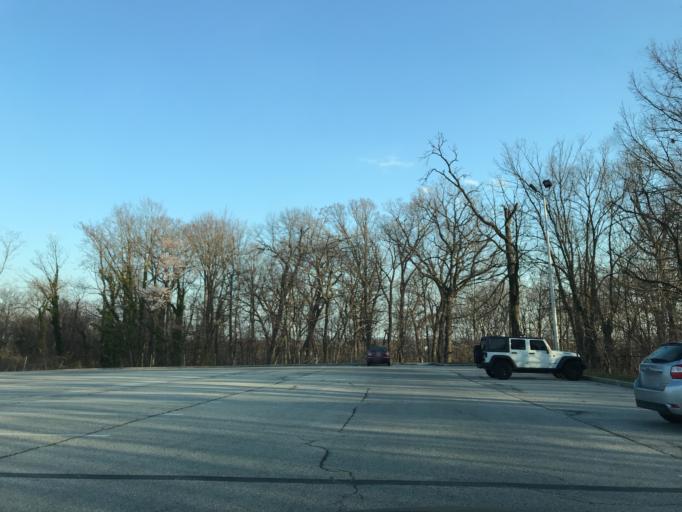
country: US
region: Maryland
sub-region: Baltimore County
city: Towson
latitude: 39.3568
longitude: -76.5859
